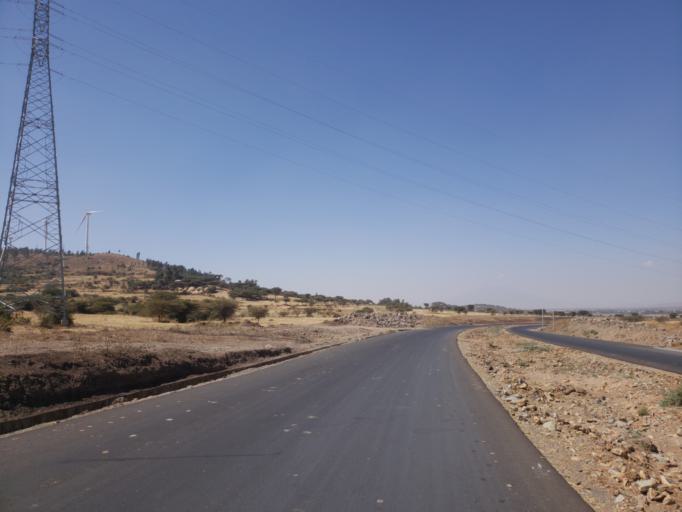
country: ET
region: Oromiya
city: Mojo
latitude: 8.5648
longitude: 39.1598
